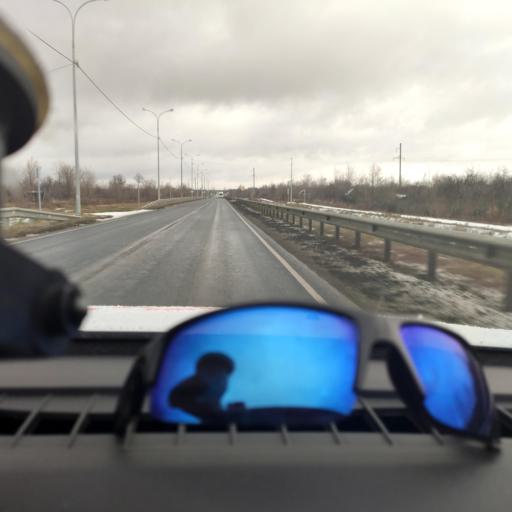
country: RU
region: Samara
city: Chapayevsk
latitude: 52.9962
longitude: 49.7428
